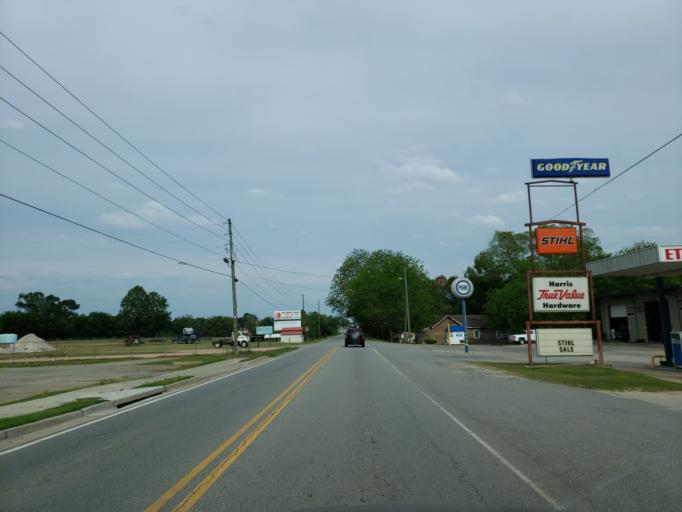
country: US
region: Georgia
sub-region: Dooly County
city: Vienna
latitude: 32.0923
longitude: -83.8031
